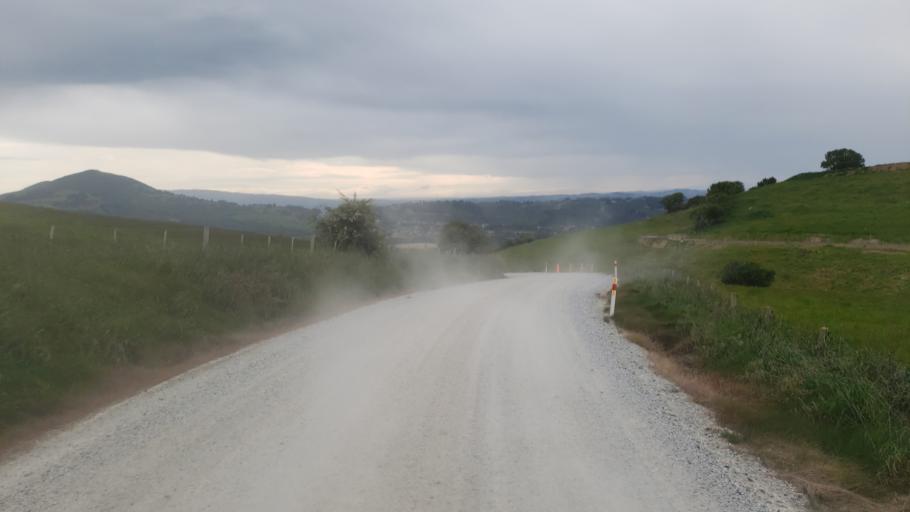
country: NZ
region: Otago
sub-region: Dunedin City
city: Dunedin
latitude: -45.9172
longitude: 170.4297
